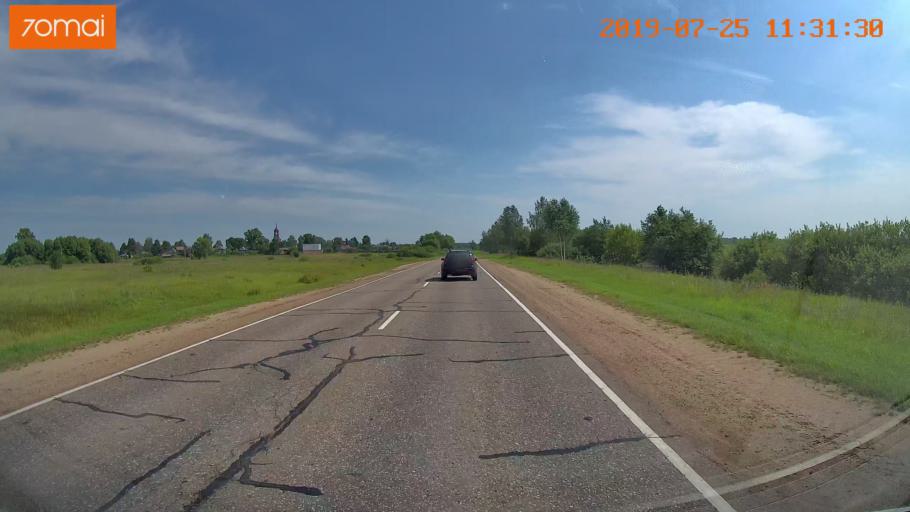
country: RU
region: Ivanovo
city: Privolzhsk
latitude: 57.3876
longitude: 41.3478
